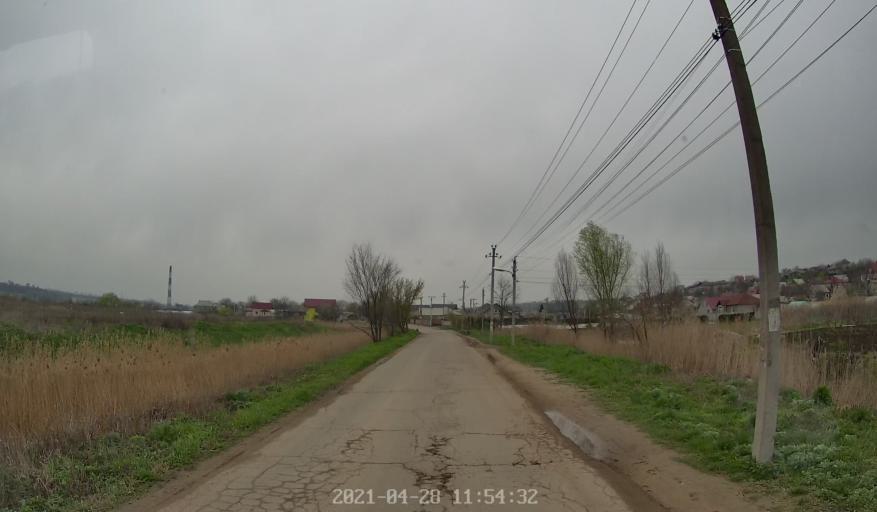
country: MD
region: Chisinau
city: Singera
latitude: 46.9611
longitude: 28.9385
